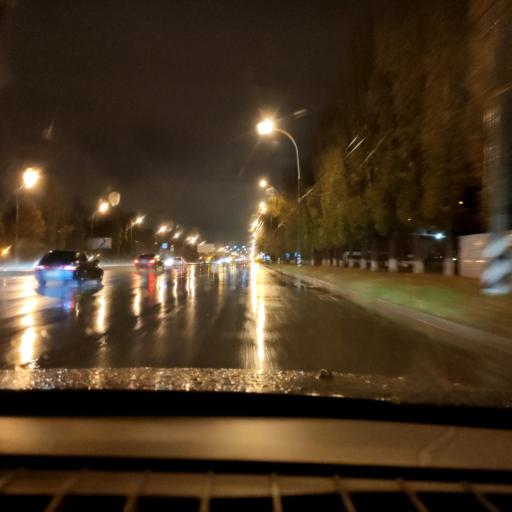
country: RU
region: Samara
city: Tol'yatti
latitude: 53.5256
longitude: 49.2810
